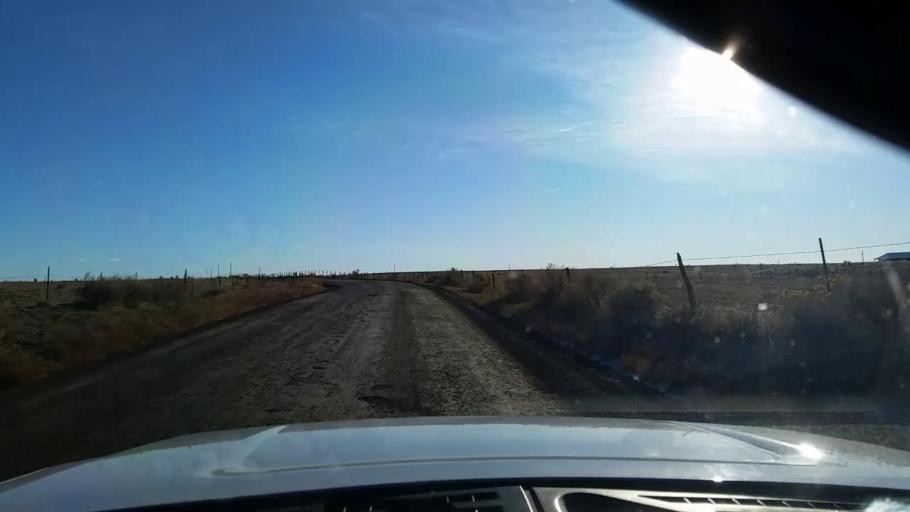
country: US
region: Colorado
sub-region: Larimer County
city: Wellington
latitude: 40.7699
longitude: -105.1159
